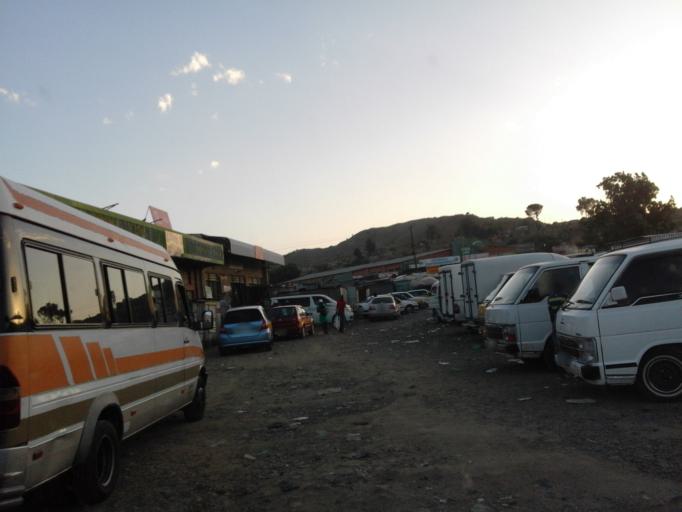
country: LS
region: Mafeteng
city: Mafeteng
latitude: -29.8224
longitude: 27.2465
